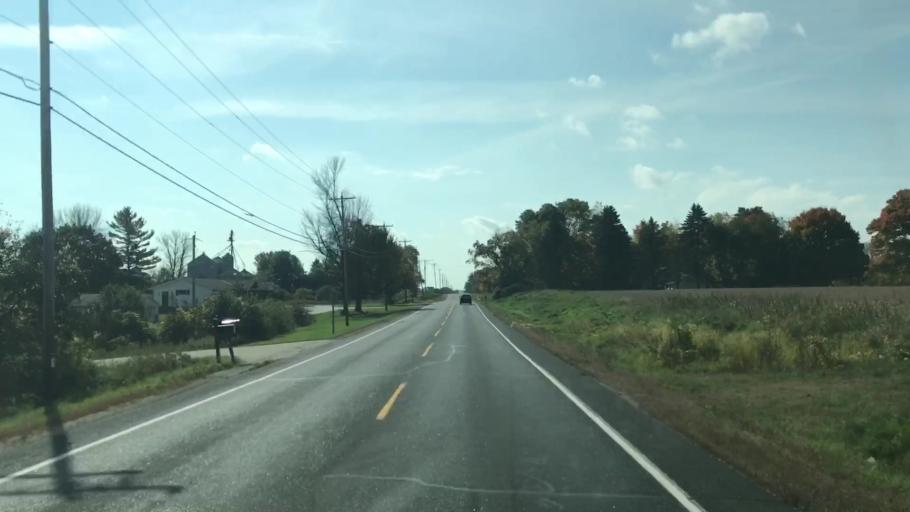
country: US
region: Wisconsin
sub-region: Ozaukee County
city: Mequon
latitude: 43.2154
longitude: -88.0435
